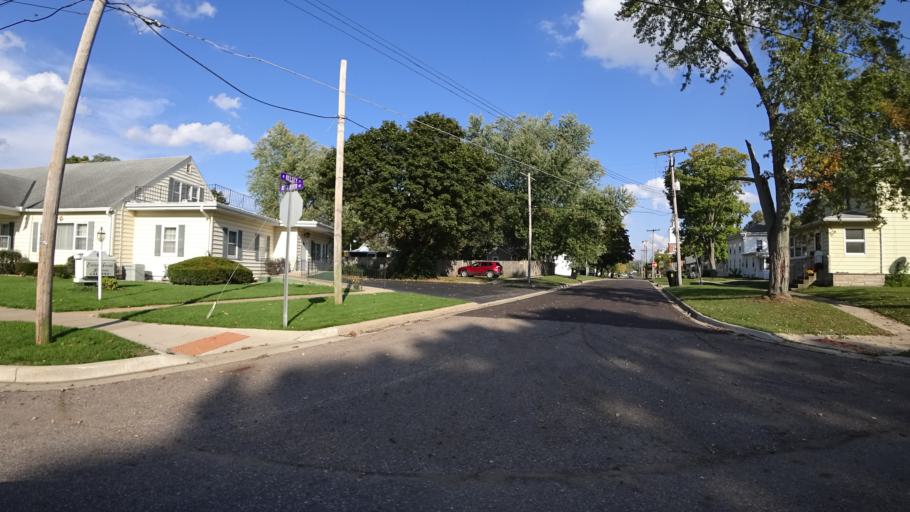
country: US
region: Michigan
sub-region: Saint Joseph County
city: Three Rivers
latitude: 41.9486
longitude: -85.6370
